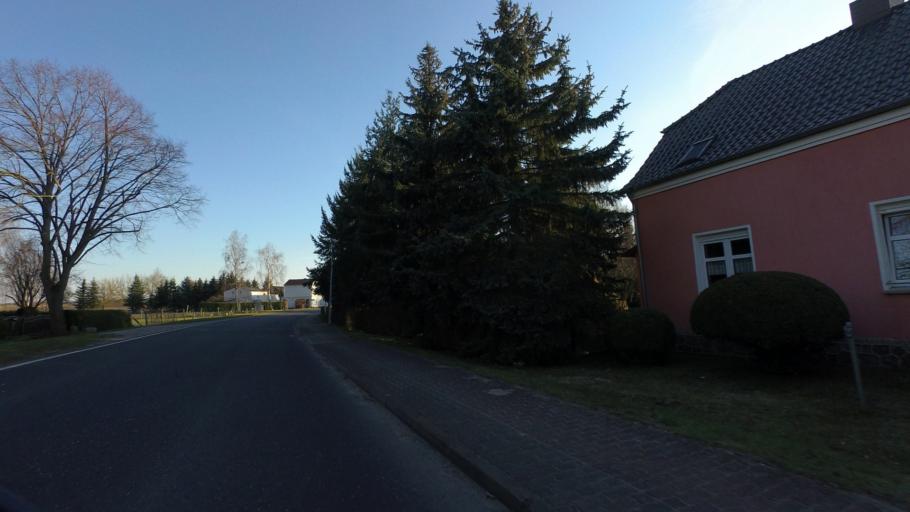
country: DE
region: Brandenburg
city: Eberswalde
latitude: 52.7437
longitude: 13.8443
